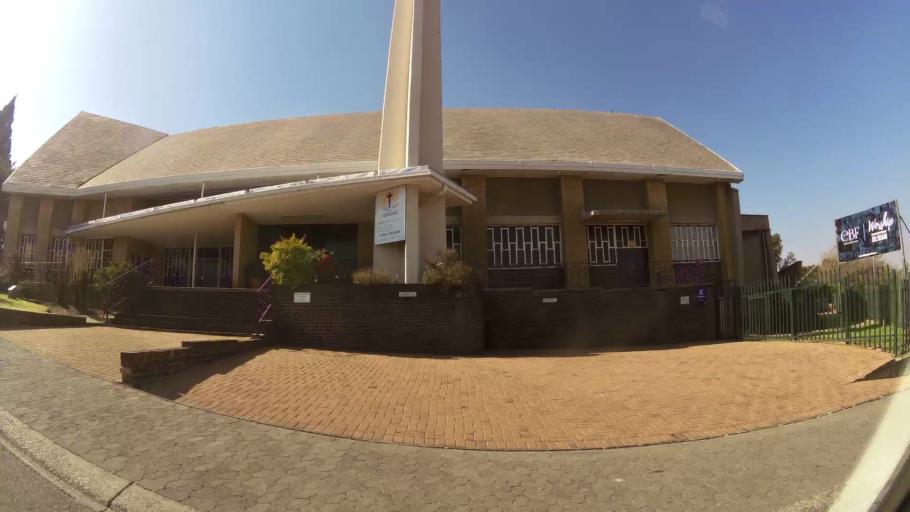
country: ZA
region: Gauteng
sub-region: City of Johannesburg Metropolitan Municipality
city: Johannesburg
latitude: -26.2611
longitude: 28.0524
